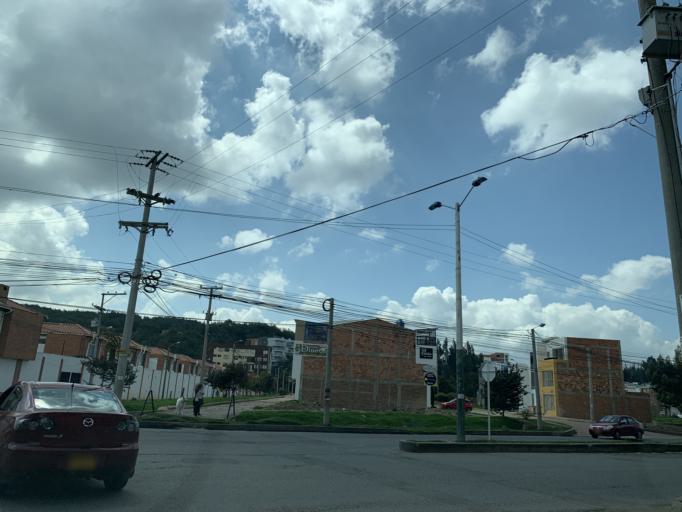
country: CO
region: Boyaca
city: Tunja
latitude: 5.5548
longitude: -73.3458
